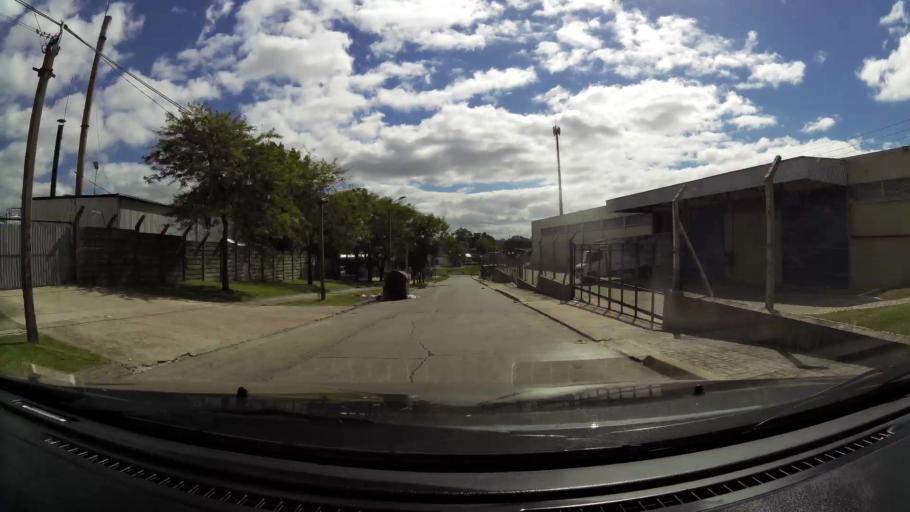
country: UY
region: Montevideo
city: Montevideo
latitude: -34.8798
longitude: -56.1345
